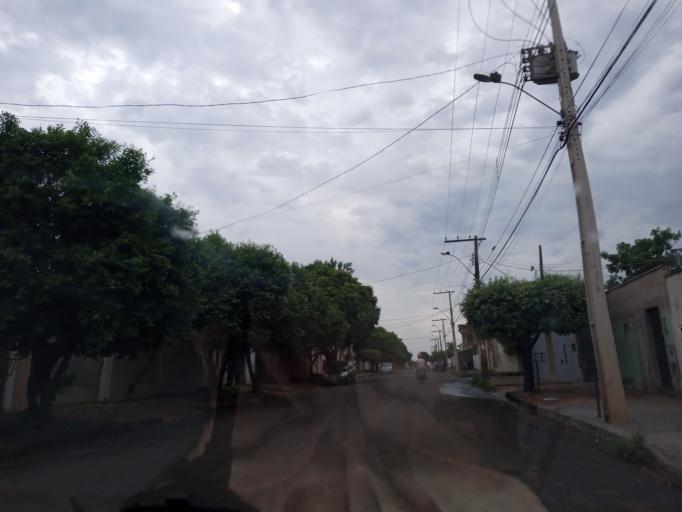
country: BR
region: Minas Gerais
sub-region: Ituiutaba
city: Ituiutaba
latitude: -18.9821
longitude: -49.4867
